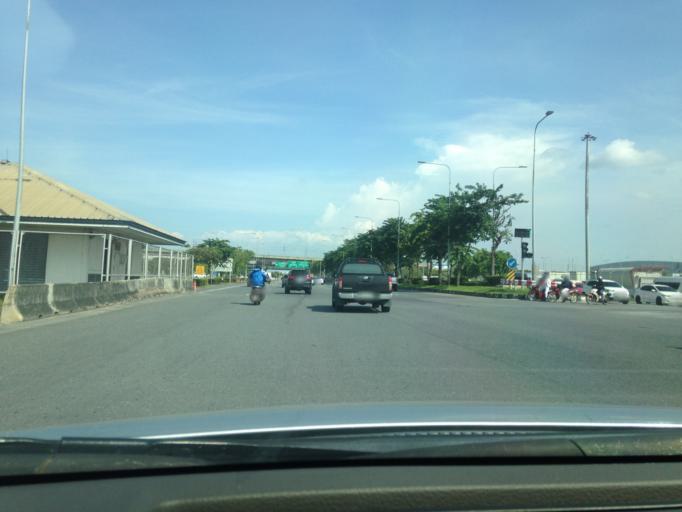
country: TH
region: Bangkok
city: Lat Krabang
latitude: 13.7141
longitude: 100.7523
